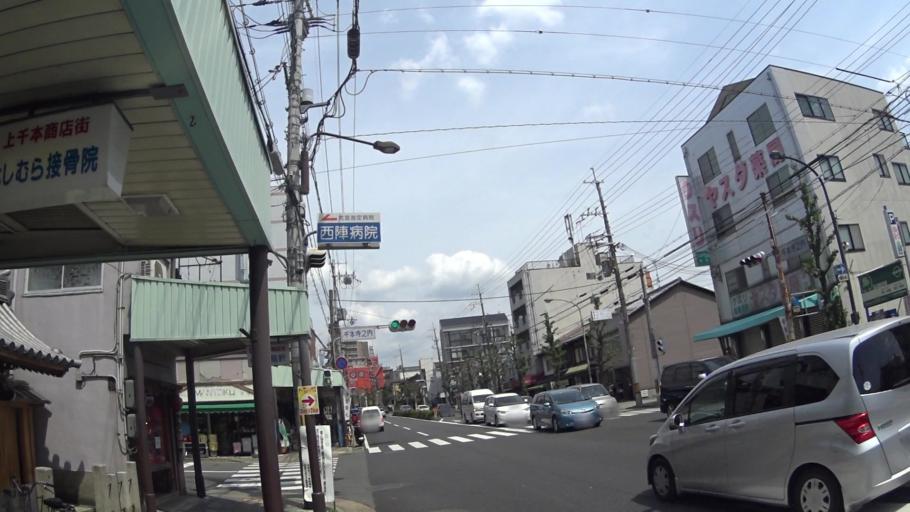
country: JP
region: Kyoto
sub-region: Kyoto-shi
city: Kamigyo-ku
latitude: 35.0342
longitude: 135.7412
